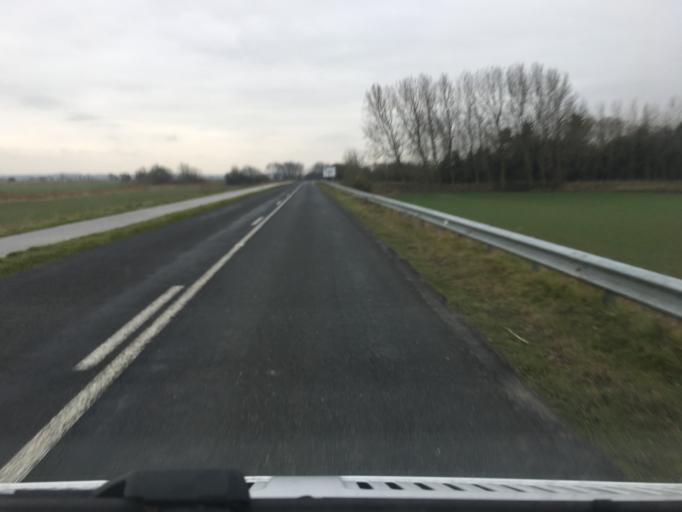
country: FR
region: Picardie
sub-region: Departement de la Somme
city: Pende
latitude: 50.2029
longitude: 1.5562
